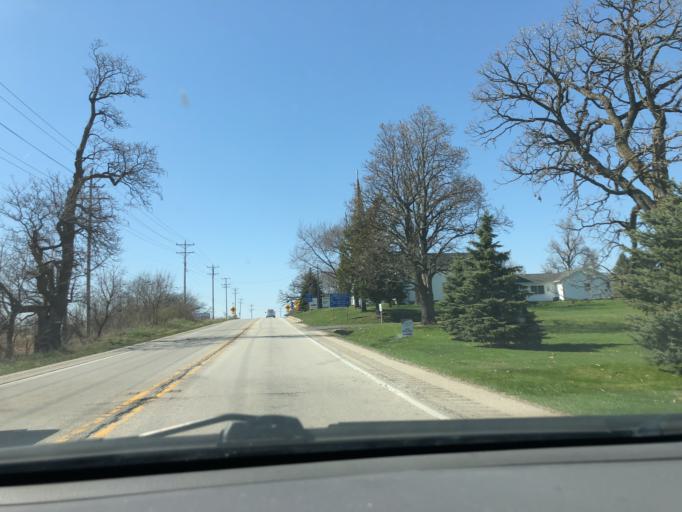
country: US
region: Illinois
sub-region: Kane County
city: Hampshire
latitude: 42.1587
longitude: -88.5241
